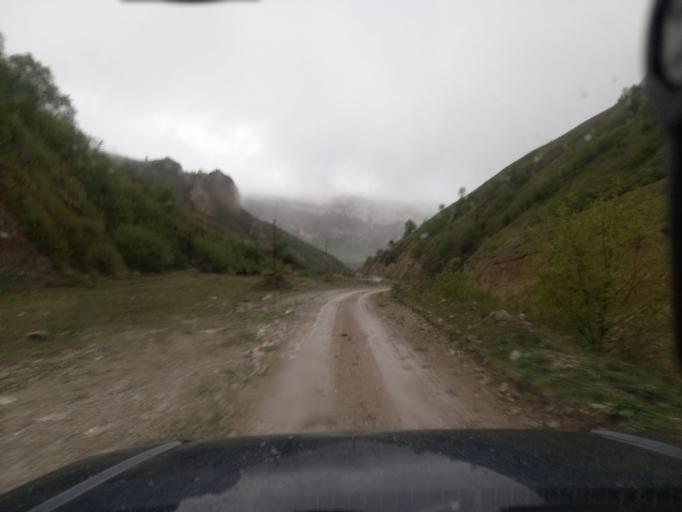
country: RU
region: Kabardino-Balkariya
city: Zhankhoteko
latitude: 43.4997
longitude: 43.1541
